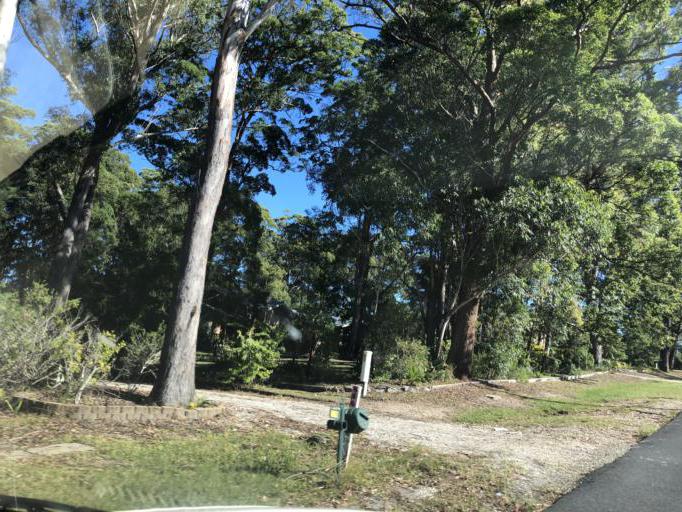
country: AU
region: New South Wales
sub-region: Nambucca Shire
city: Macksville
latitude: -30.6795
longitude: 152.9621
